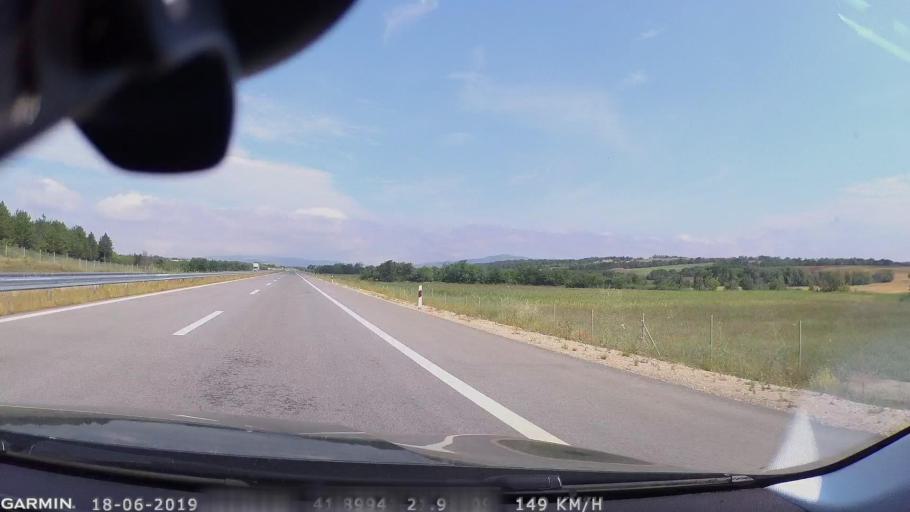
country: MK
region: Sveti Nikole
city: Gorobinci
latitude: 41.9008
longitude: 21.9155
